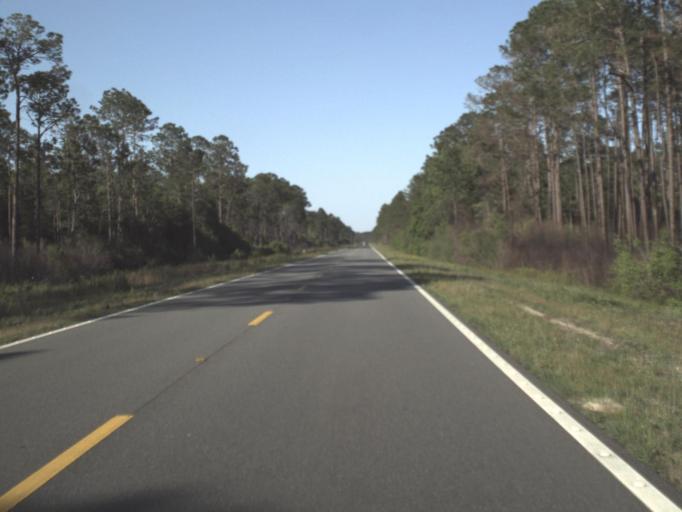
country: US
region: Florida
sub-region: Liberty County
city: Bristol
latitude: 30.1968
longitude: -84.9179
